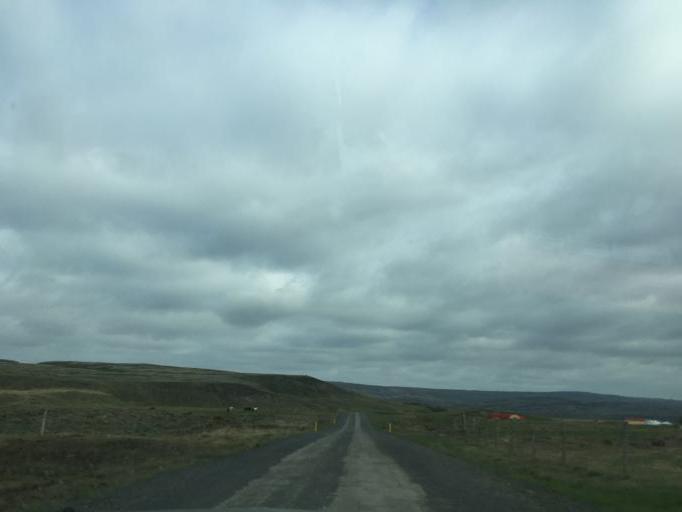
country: IS
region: South
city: Selfoss
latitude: 64.2911
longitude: -20.2335
